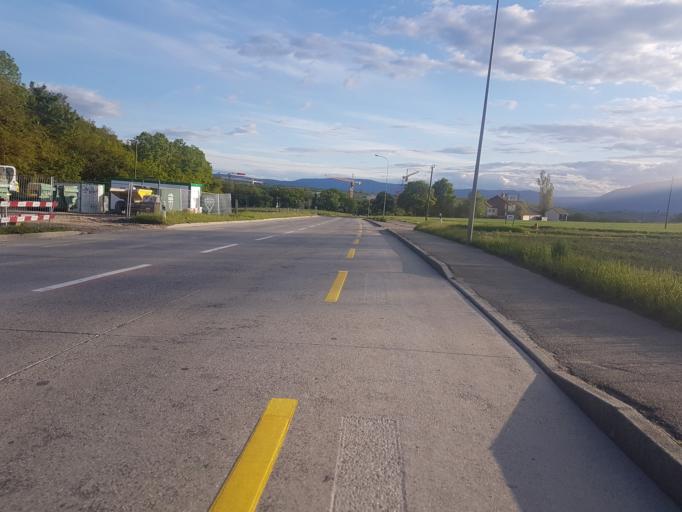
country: CH
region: Geneva
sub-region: Geneva
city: Vernier
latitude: 46.2048
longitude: 6.0643
